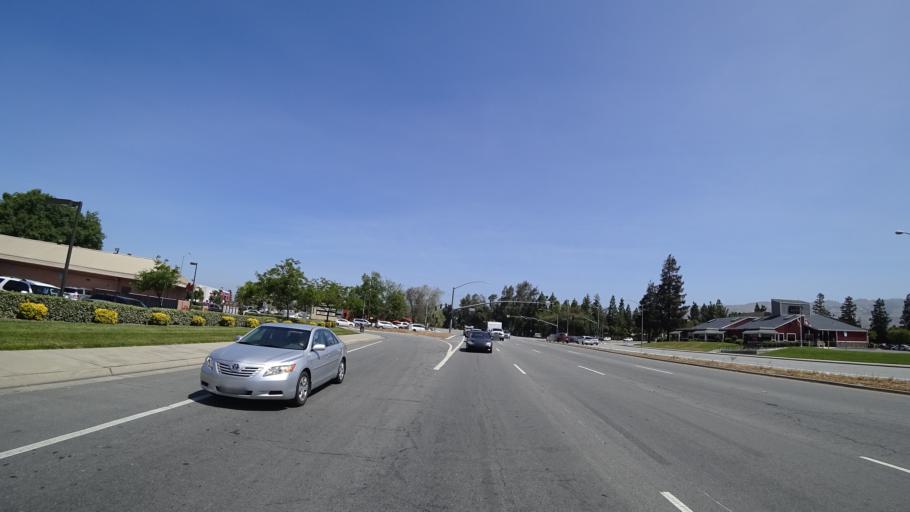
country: US
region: California
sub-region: Santa Clara County
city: Seven Trees
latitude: 37.3107
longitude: -121.8086
